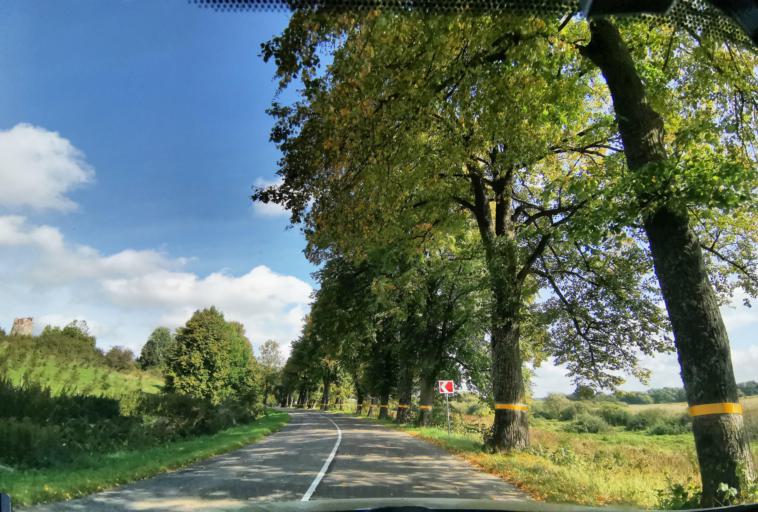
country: RU
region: Kaliningrad
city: Chernyakhovsk
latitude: 54.6511
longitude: 21.7857
